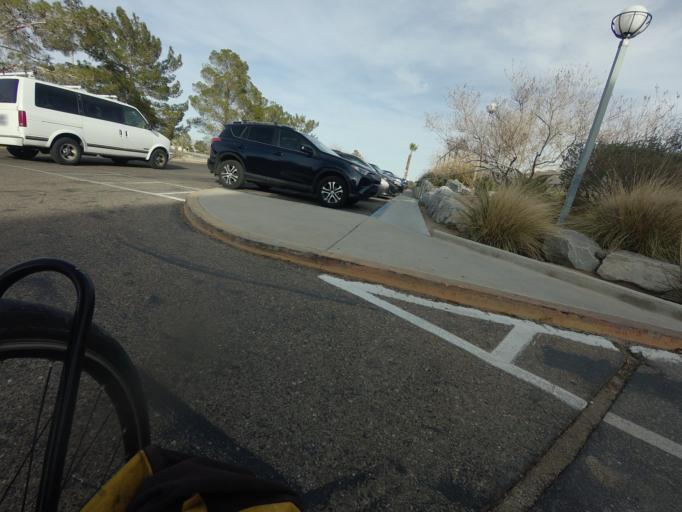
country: US
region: California
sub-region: Kern County
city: Ridgecrest
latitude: 35.6420
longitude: -117.6713
